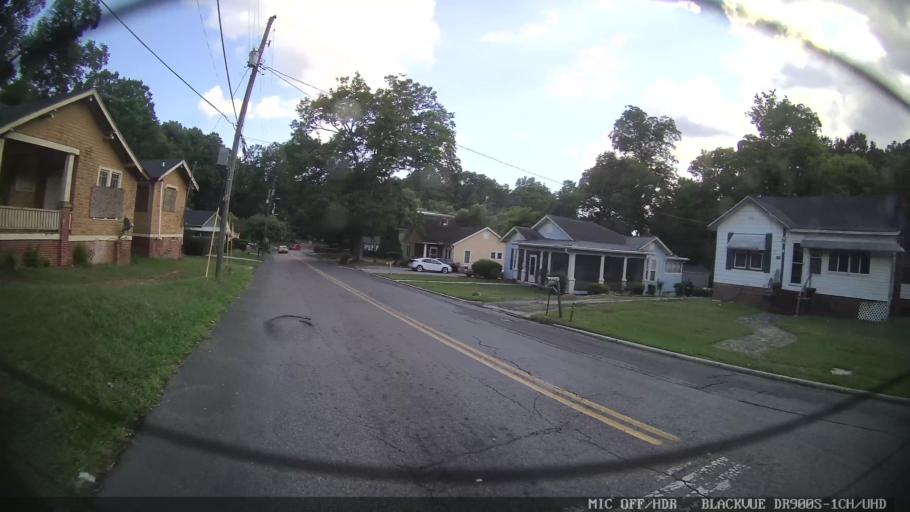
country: US
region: Georgia
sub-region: Floyd County
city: Rome
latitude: 34.2638
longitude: -85.1613
